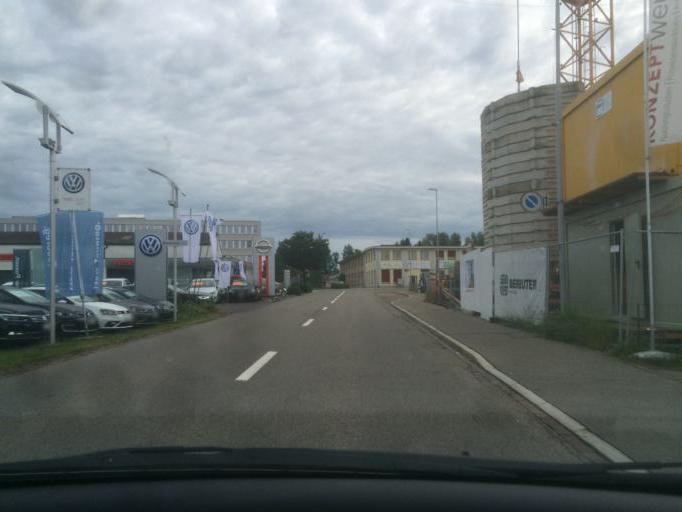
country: CH
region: Zurich
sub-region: Bezirk Hinwil
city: Wetzikon / Robenhausen
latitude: 47.3315
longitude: 8.7913
